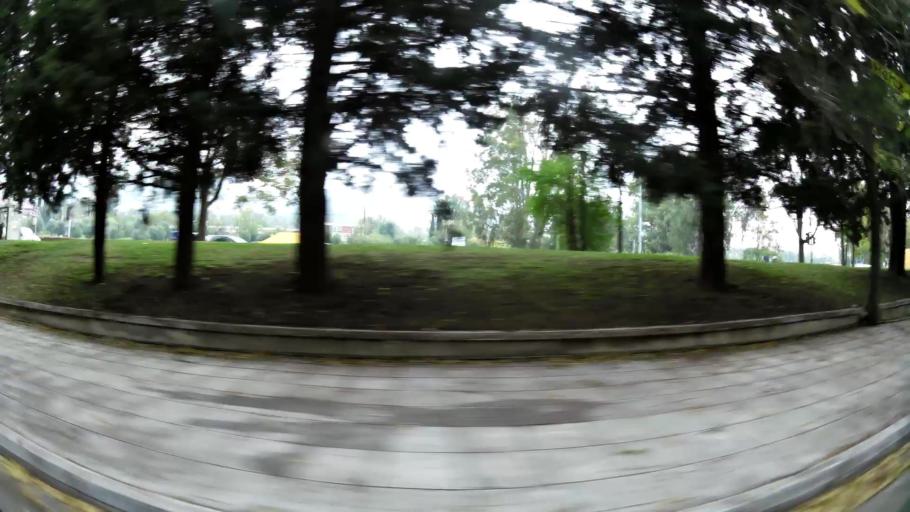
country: GR
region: Attica
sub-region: Nomarchia Athinas
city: Chaidari
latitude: 38.0122
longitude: 23.6399
